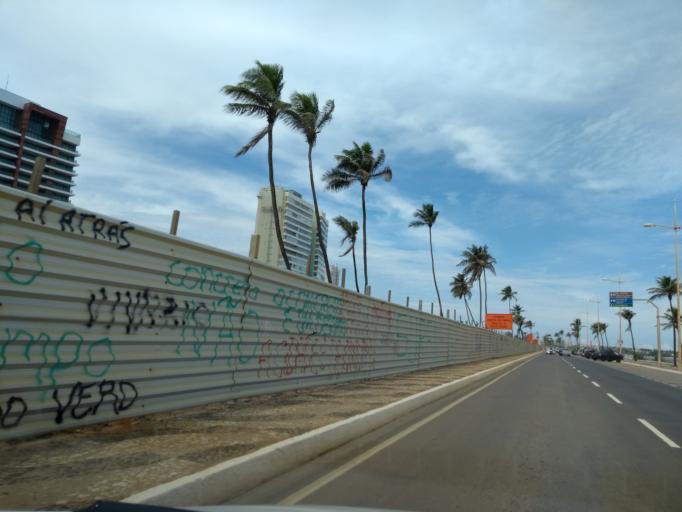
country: BR
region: Bahia
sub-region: Lauro De Freitas
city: Lauro de Freitas
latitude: -12.9601
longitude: -38.3952
